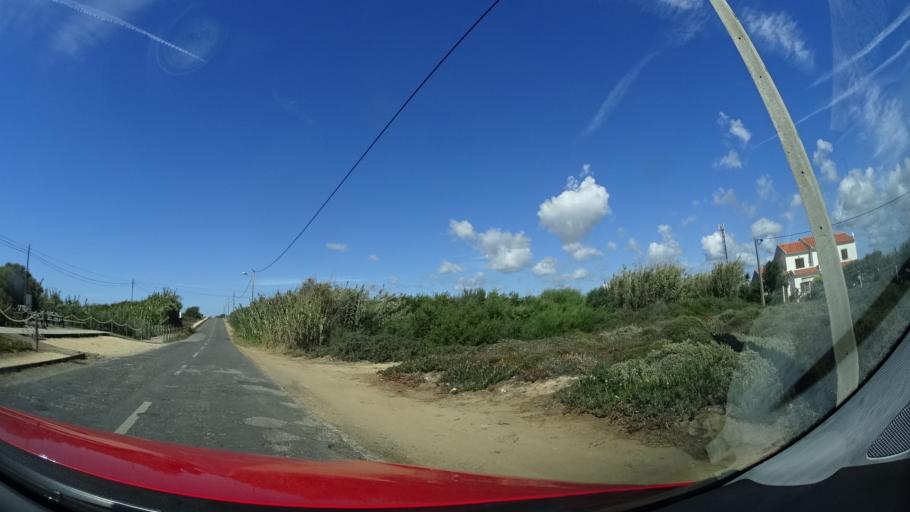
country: PT
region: Beja
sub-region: Odemira
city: Sao Teotonio
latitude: 37.5310
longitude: -8.7843
